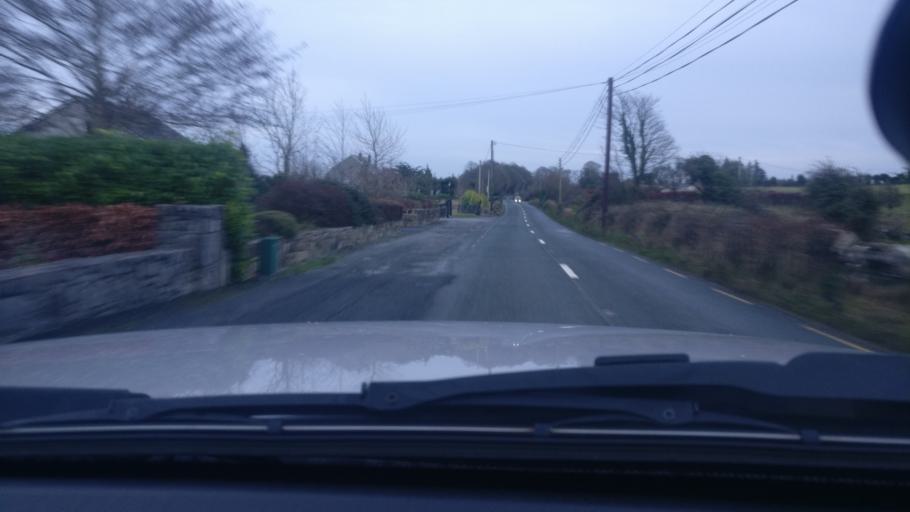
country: IE
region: Connaught
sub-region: County Galway
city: Loughrea
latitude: 53.1742
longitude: -8.5310
